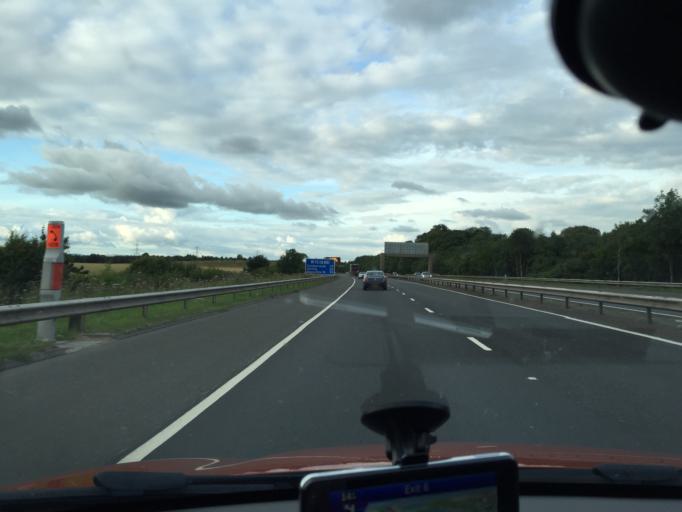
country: GB
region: Scotland
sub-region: South Lanarkshire
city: Uddingston
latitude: 55.8619
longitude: -4.0835
